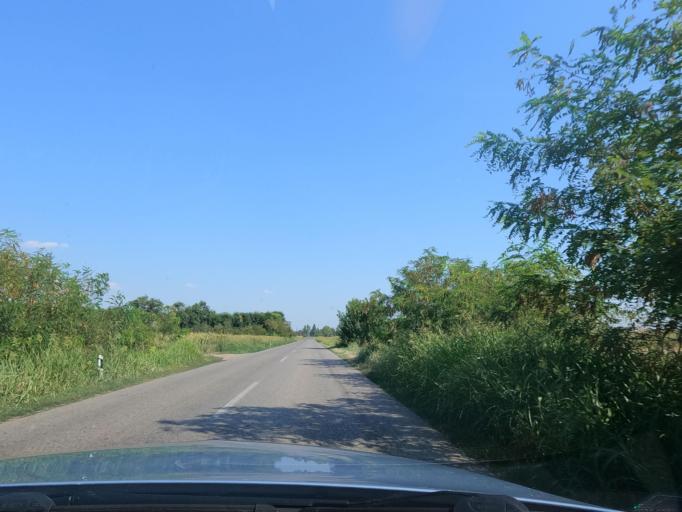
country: RS
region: Autonomna Pokrajina Vojvodina
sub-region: Juznobacki Okrug
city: Becej
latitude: 45.6361
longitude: 20.0060
